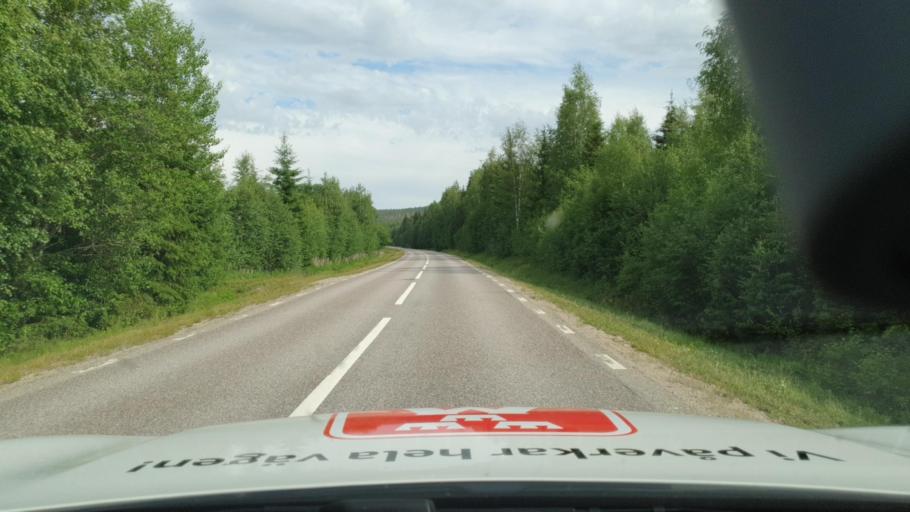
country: NO
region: Hedmark
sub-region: Trysil
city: Innbygda
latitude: 60.9046
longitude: 12.5664
